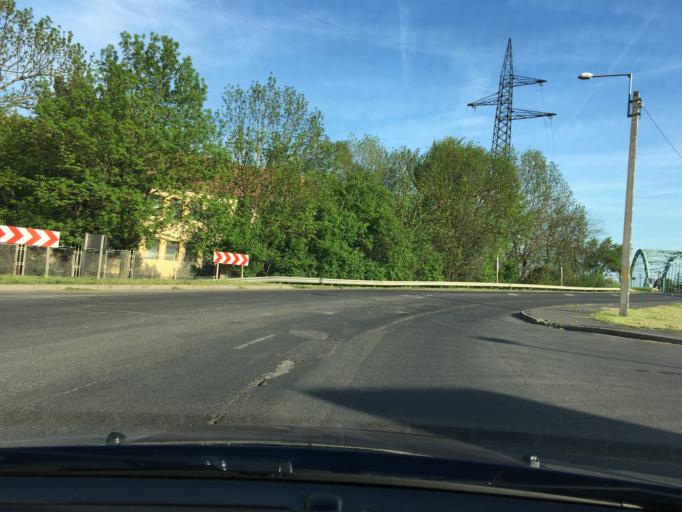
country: HU
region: Bekes
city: Szeghalom
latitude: 47.0149
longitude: 21.1782
